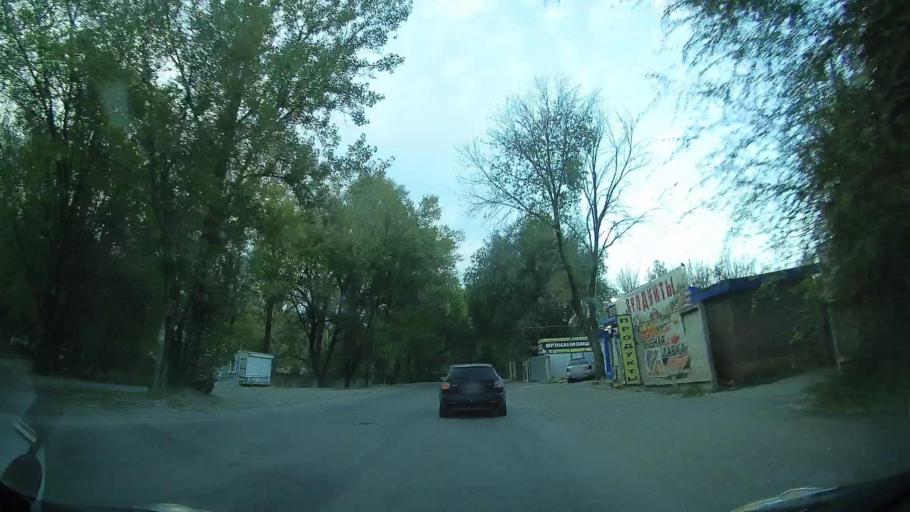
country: RU
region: Rostov
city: Severnyy
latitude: 47.2695
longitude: 39.6608
